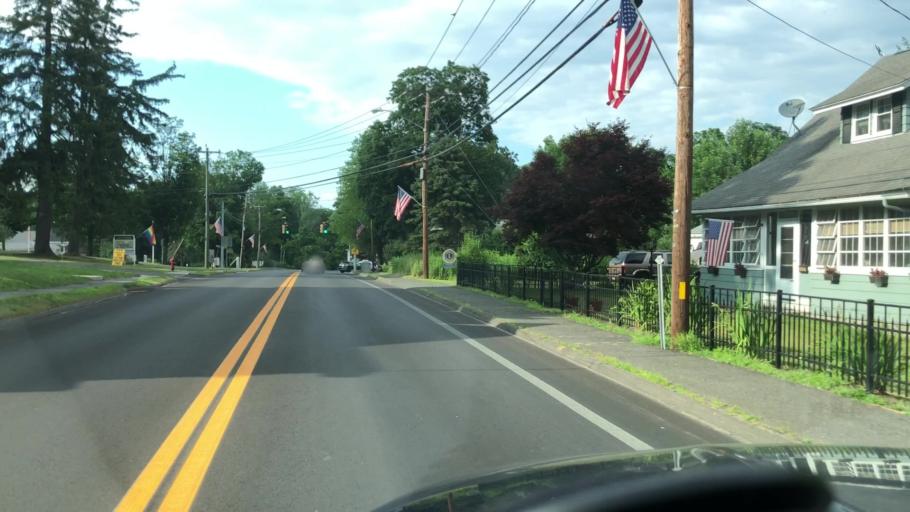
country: US
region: Massachusetts
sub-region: Hampshire County
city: Southampton
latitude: 42.2283
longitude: -72.7300
